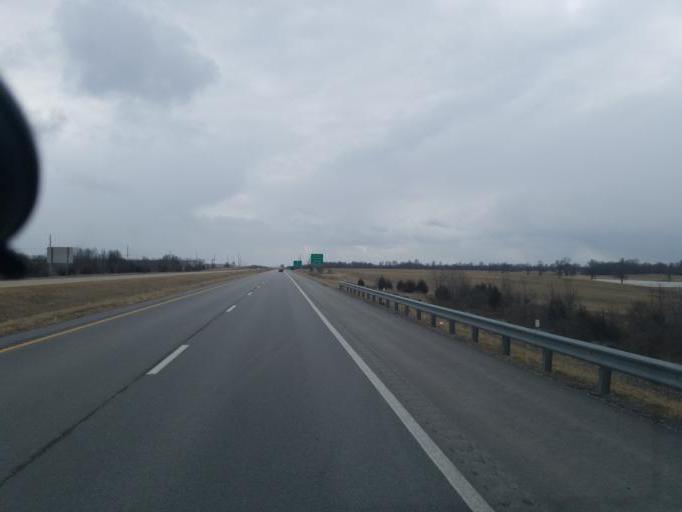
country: US
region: Missouri
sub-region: Randolph County
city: Moberly
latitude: 39.4070
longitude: -92.4126
